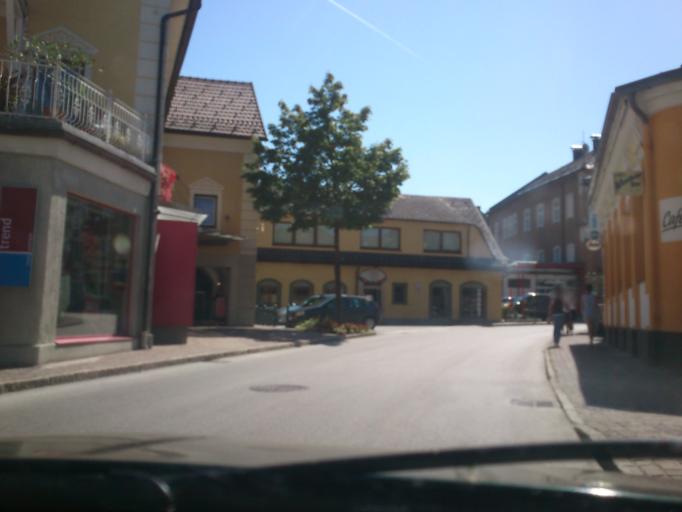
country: AT
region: Upper Austria
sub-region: Politischer Bezirk Kirchdorf an der Krems
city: Rossleithen
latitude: 47.7225
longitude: 14.3278
